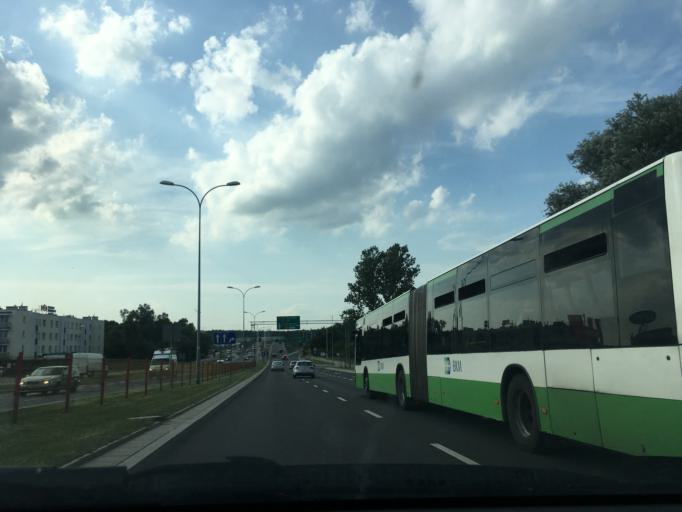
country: PL
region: Podlasie
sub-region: Bialystok
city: Bialystok
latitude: 53.1556
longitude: 23.1581
